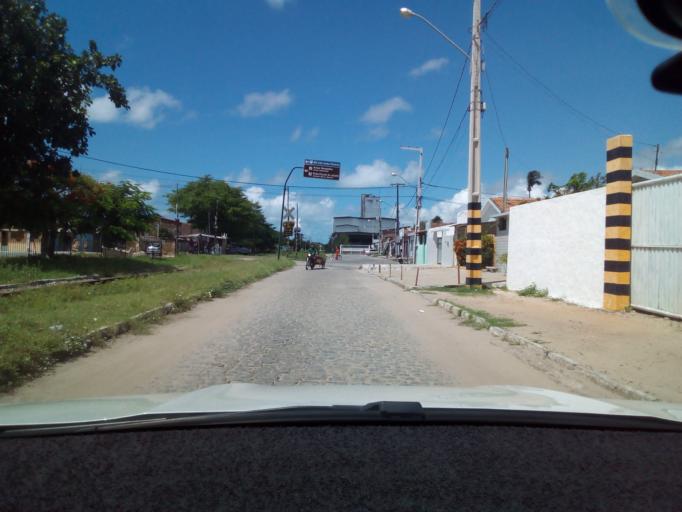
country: BR
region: Paraiba
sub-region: Cabedelo
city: Cabedelo
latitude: -6.9809
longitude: -34.8346
